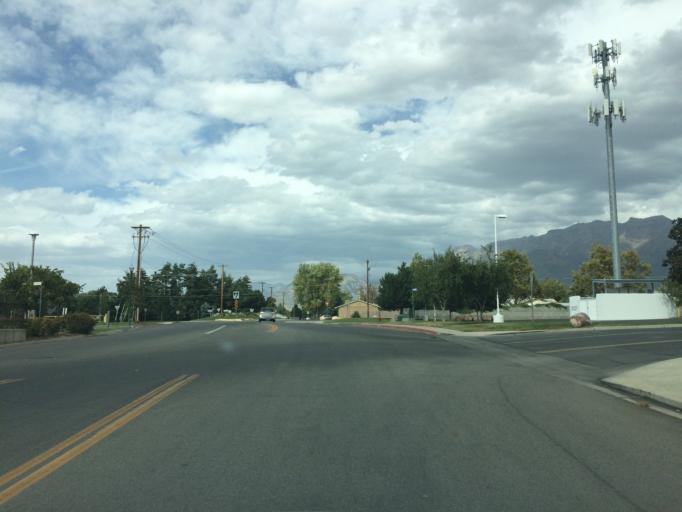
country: US
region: Utah
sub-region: Utah County
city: Orem
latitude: 40.2743
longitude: -111.7045
